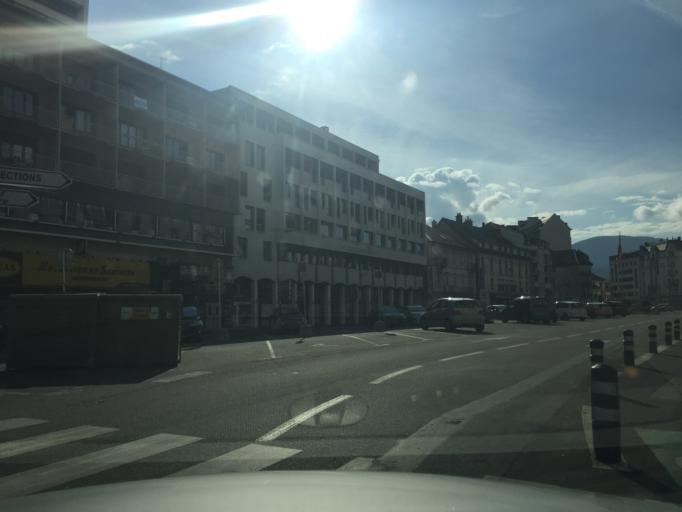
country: FR
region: Rhone-Alpes
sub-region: Departement de la Savoie
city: Chambery
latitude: 45.5683
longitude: 5.9213
